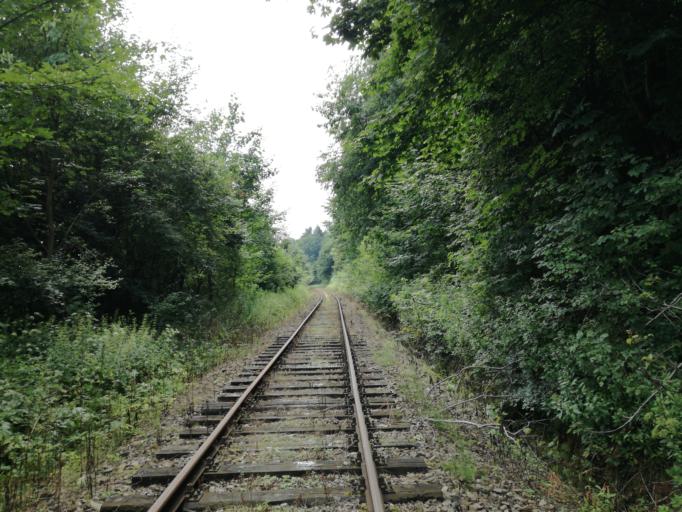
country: PL
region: Subcarpathian Voivodeship
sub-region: Powiat leski
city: Uherce Mineralne
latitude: 49.4598
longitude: 22.3877
